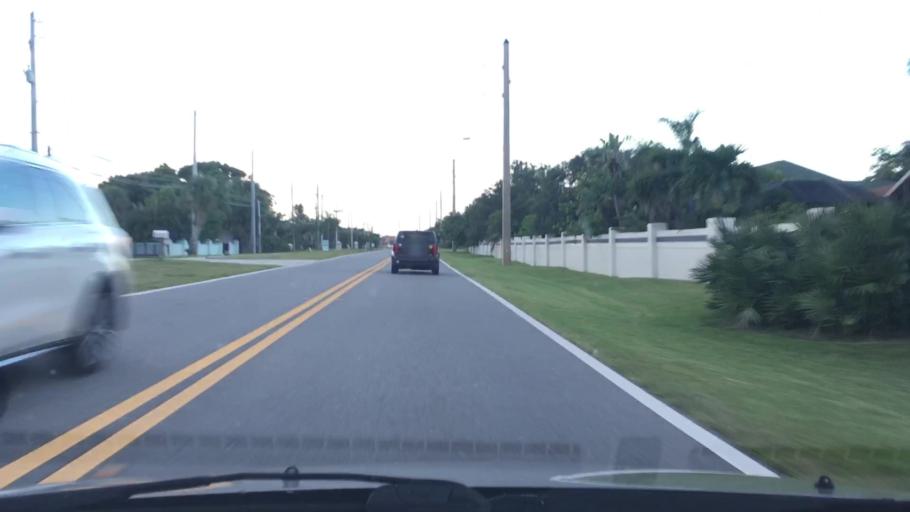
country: US
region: Florida
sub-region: Brevard County
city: Indian Harbour Beach
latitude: 28.1265
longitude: -80.5898
